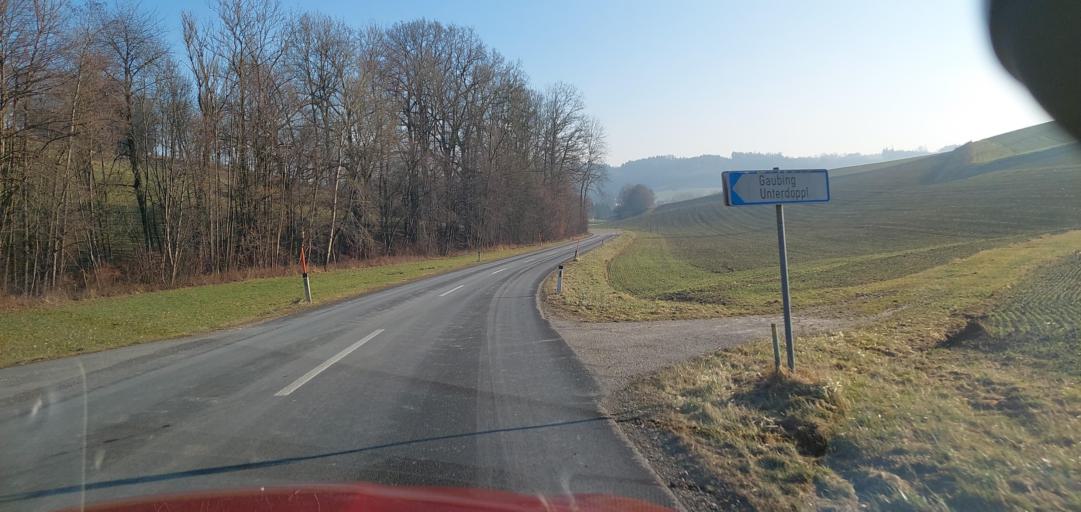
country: AT
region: Upper Austria
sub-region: Wels-Land
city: Offenhausen
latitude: 48.1849
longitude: 13.8533
